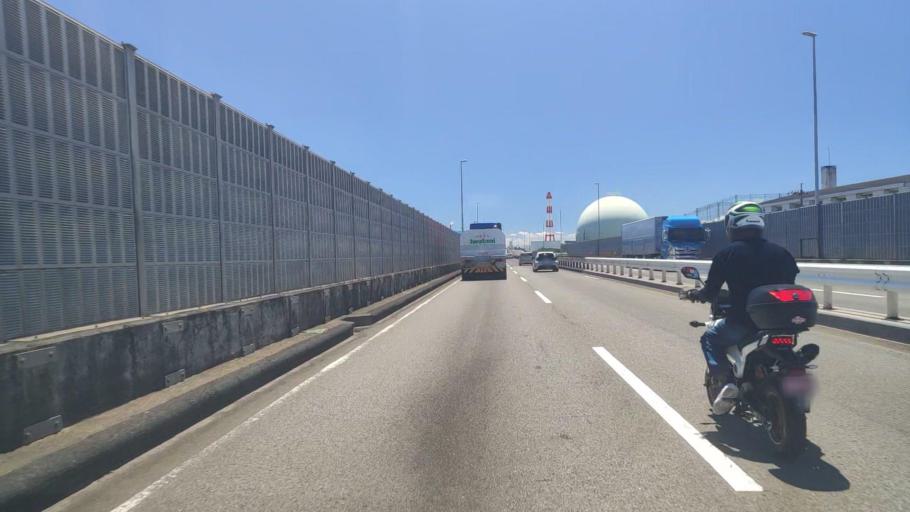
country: JP
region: Mie
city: Yokkaichi
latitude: 34.9515
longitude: 136.6240
